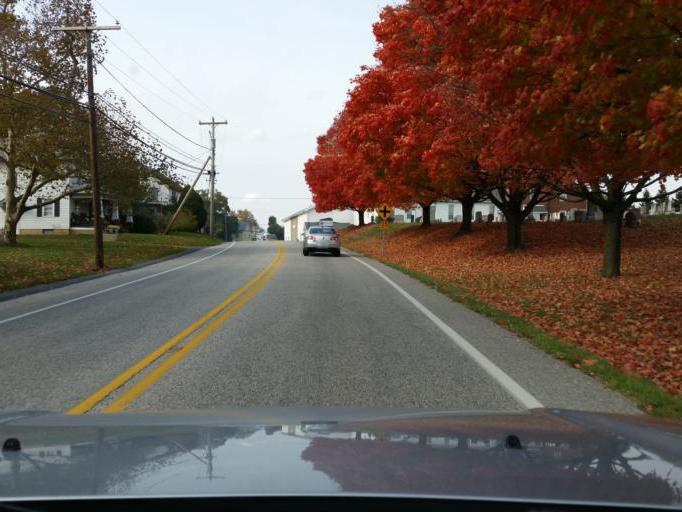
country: US
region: Pennsylvania
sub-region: Dauphin County
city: Skyline View
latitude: 40.3199
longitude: -76.7028
